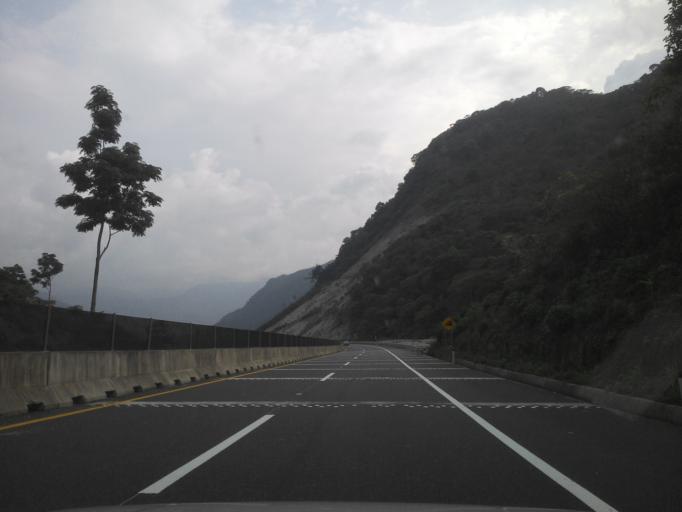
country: MX
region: Puebla
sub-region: Xicotepec
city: San Lorenzo
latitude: 20.3753
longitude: -97.9468
